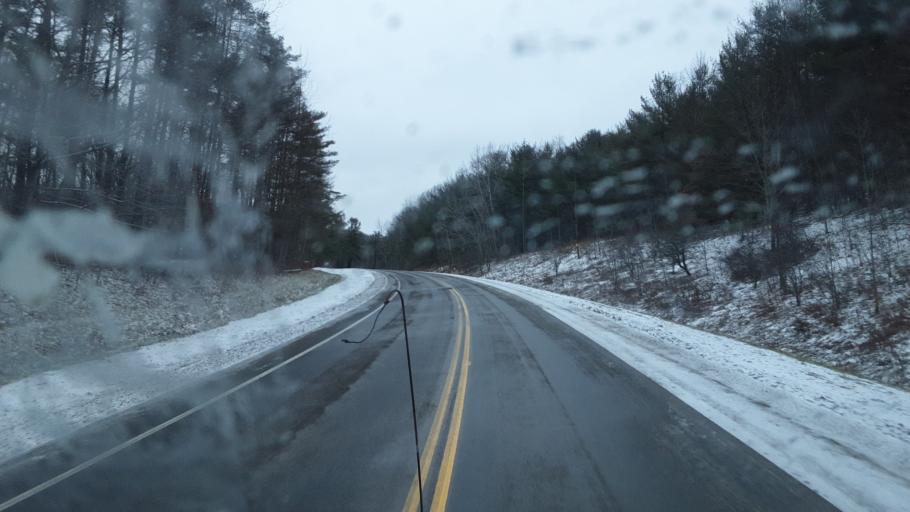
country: US
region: New York
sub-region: Allegany County
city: Friendship
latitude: 42.2208
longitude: -78.1422
